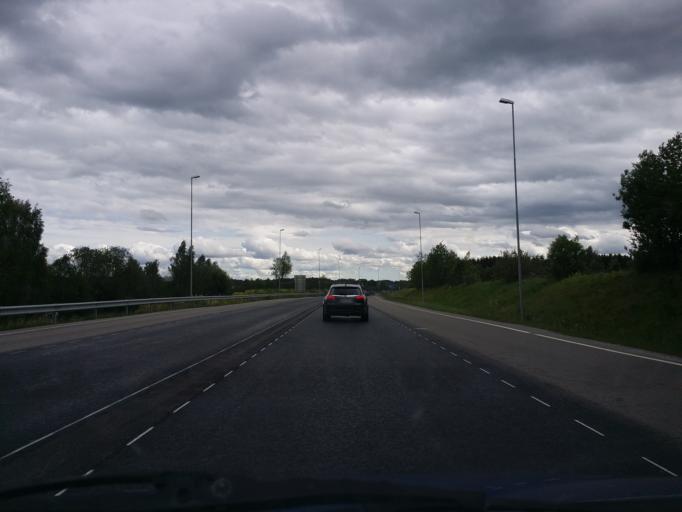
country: NO
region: Hedmark
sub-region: Hamar
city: Hamar
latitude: 60.8325
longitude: 11.0810
